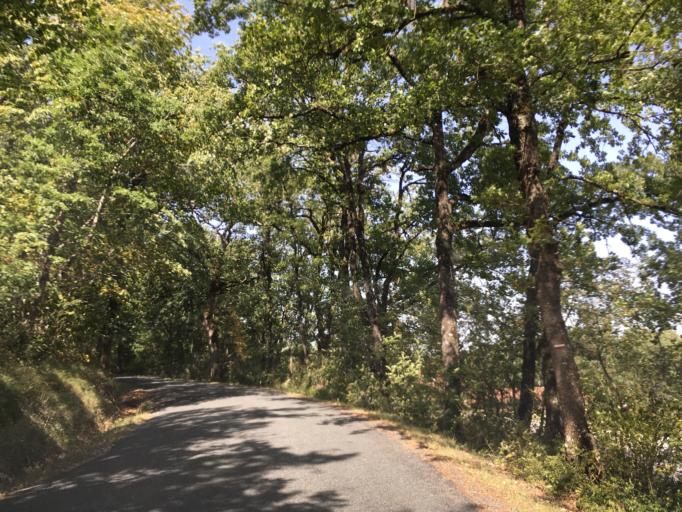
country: FR
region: Midi-Pyrenees
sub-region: Departement du Tarn
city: Lagarrigue
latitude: 43.5931
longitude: 2.3139
